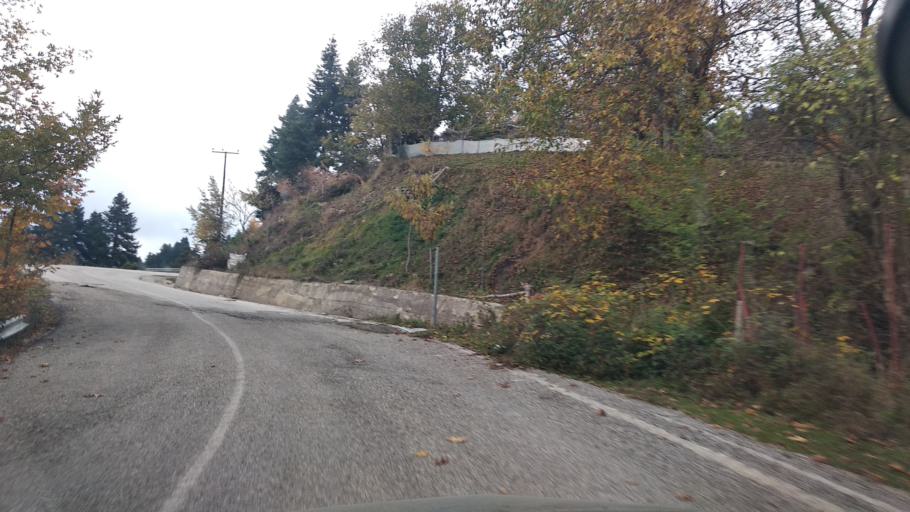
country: GR
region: Thessaly
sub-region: Trikala
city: Kalampaka
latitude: 39.5887
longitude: 21.4904
